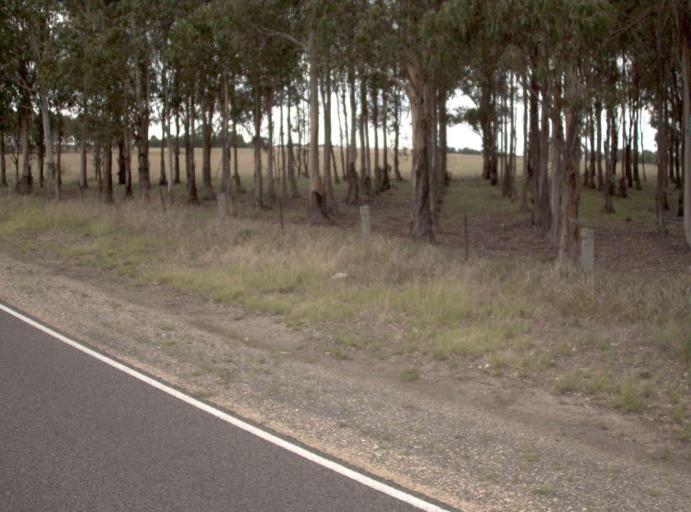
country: AU
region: Victoria
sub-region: East Gippsland
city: Bairnsdale
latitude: -37.9668
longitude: 147.4823
